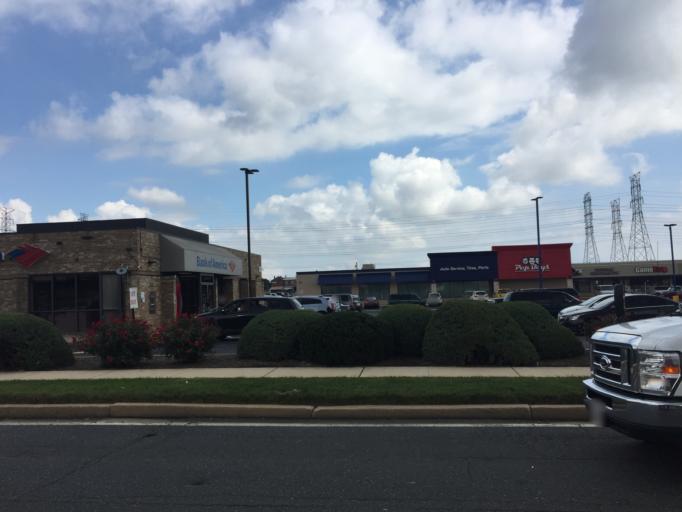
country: US
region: Maryland
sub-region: Baltimore County
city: Dundalk
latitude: 39.2749
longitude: -76.5033
